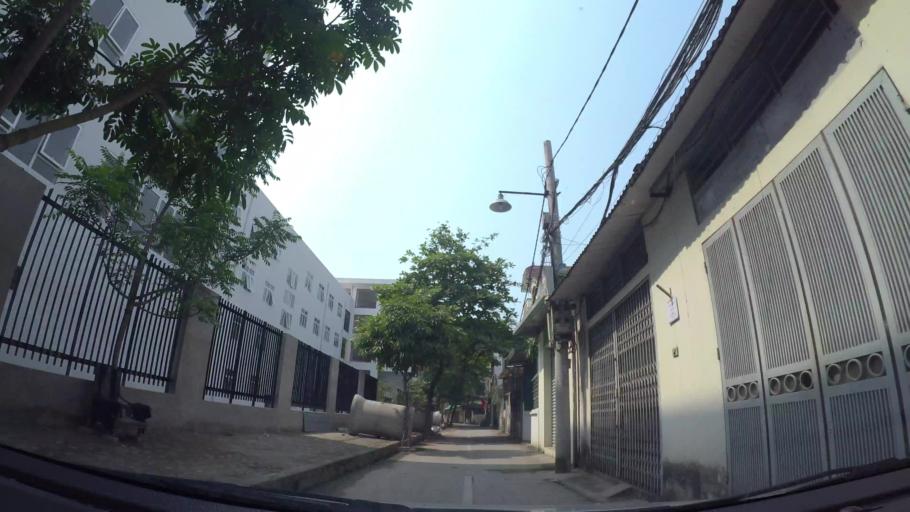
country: VN
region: Ha Noi
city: Tay Ho
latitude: 21.0869
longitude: 105.8103
